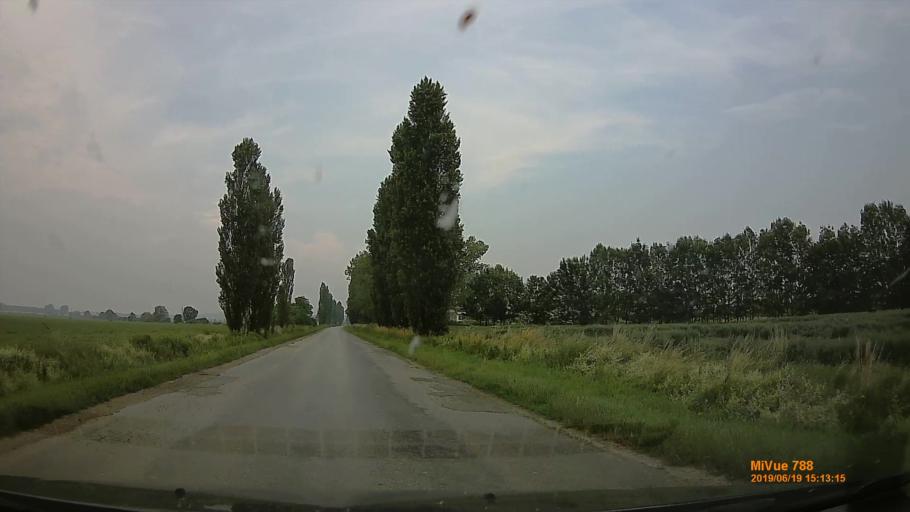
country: HU
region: Baranya
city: Szigetvar
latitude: 46.0594
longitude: 17.8138
